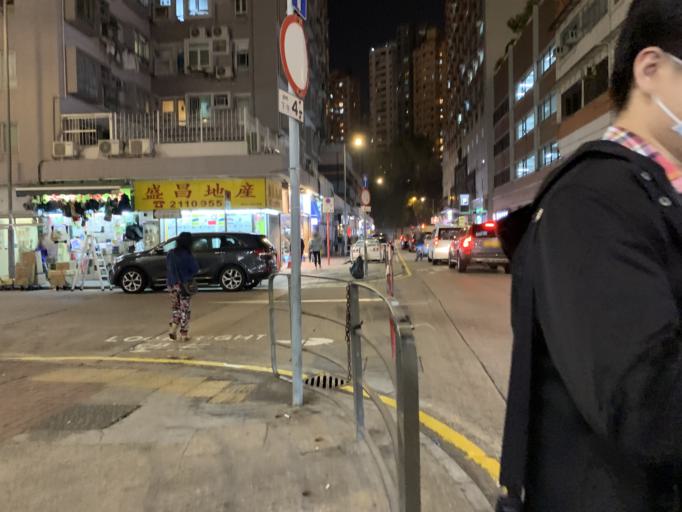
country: HK
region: Kowloon City
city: Kowloon
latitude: 22.3164
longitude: 114.1732
